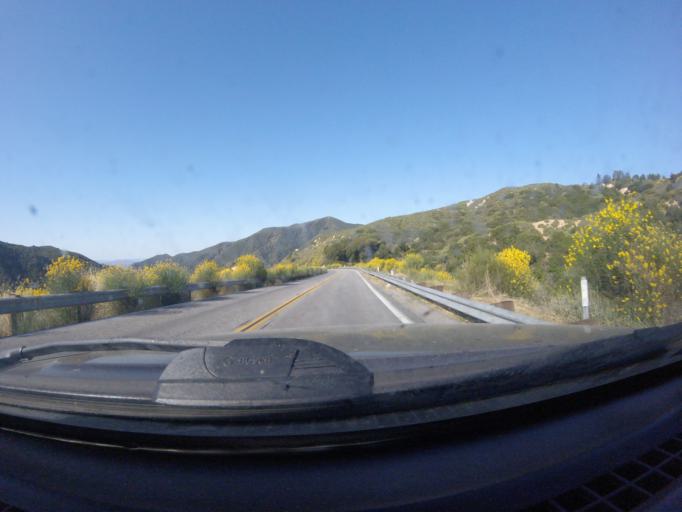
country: US
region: California
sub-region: San Bernardino County
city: Running Springs
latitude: 34.1840
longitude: -117.1410
